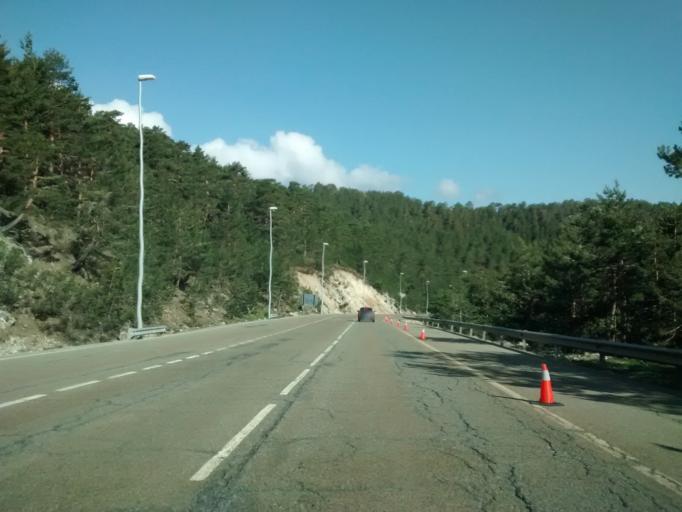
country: ES
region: Madrid
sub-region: Provincia de Madrid
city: Navacerrada
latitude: 40.7901
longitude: -4.0051
